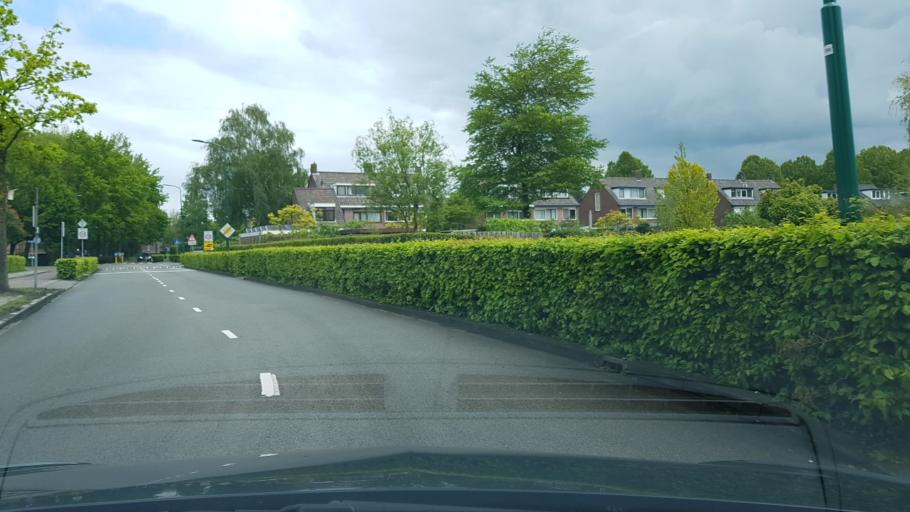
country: NL
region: North Holland
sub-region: Gemeente Blaricum
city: Blaricum
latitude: 52.2499
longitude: 5.2619
